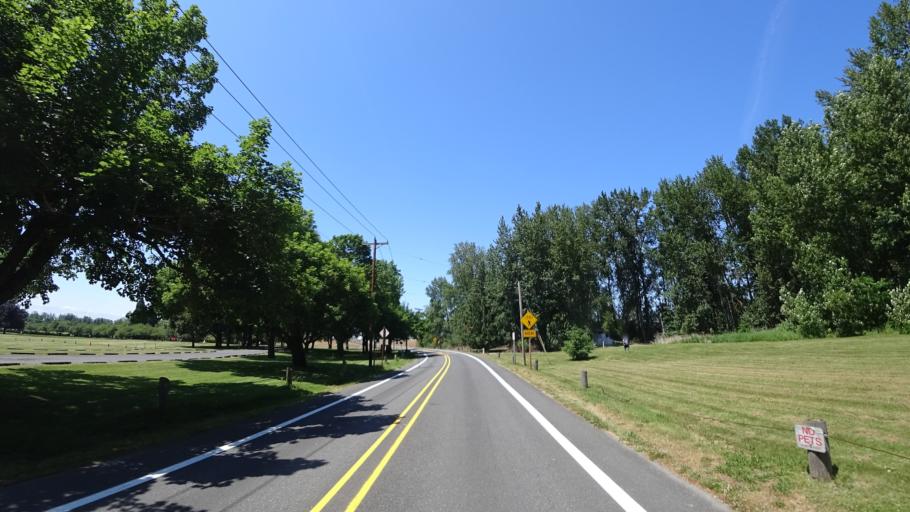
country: US
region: Oregon
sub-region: Multnomah County
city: Fairview
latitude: 45.5575
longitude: -122.4473
